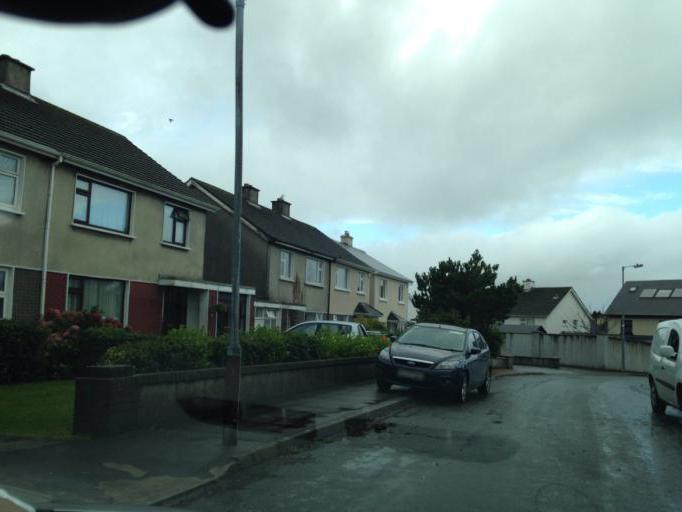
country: IE
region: Connaught
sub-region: County Galway
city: Gaillimh
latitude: 53.2743
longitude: -9.0216
